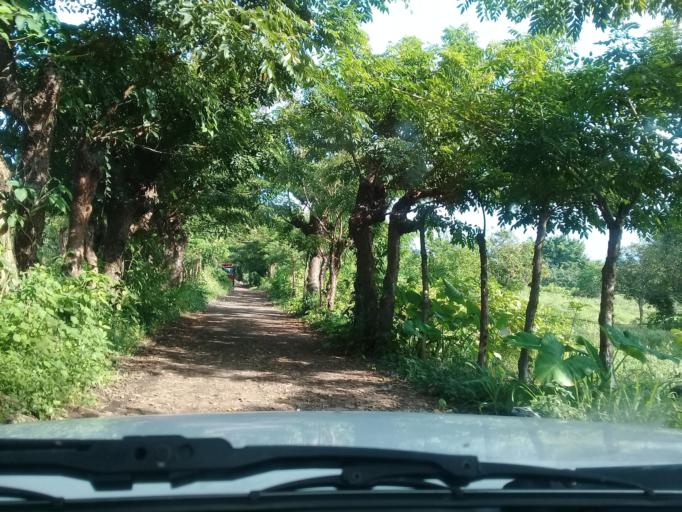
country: MX
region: Veracruz
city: Catemaco
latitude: 18.4324
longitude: -95.1239
